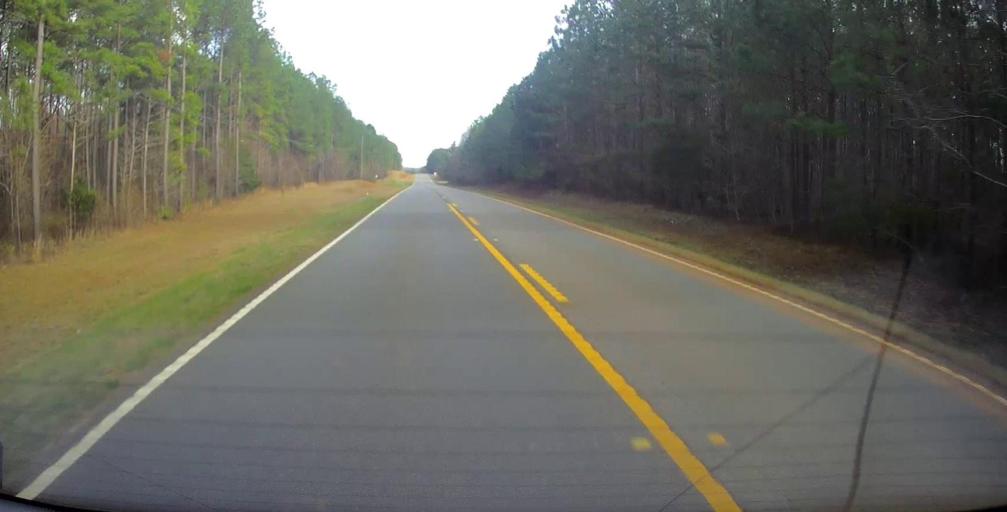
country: US
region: Georgia
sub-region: Harris County
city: Hamilton
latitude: 32.6903
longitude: -84.7877
